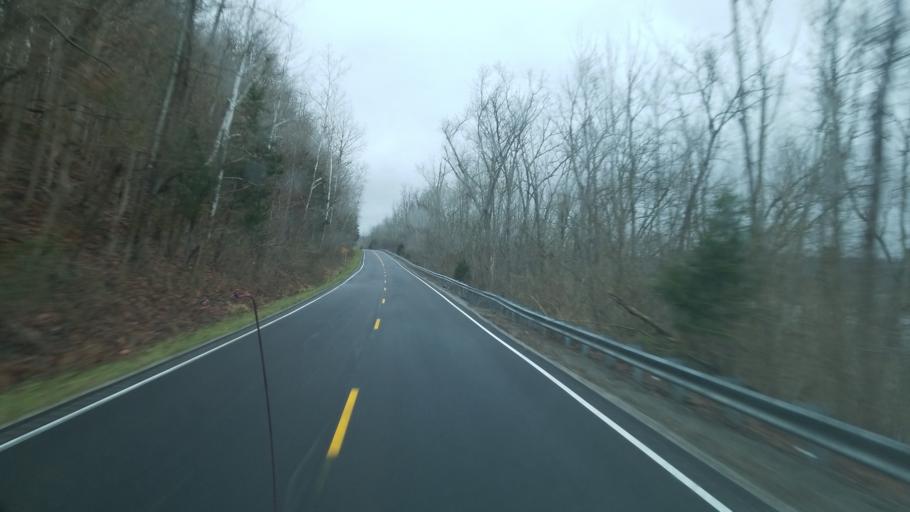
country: US
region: Kentucky
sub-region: Bracken County
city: Augusta
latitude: 38.7740
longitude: -83.9364
